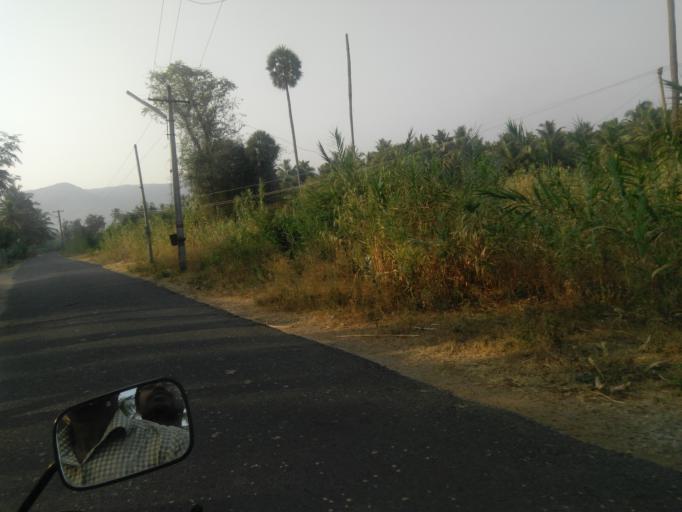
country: IN
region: Tamil Nadu
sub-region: Coimbatore
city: Karamadai
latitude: 11.2156
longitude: 76.8882
